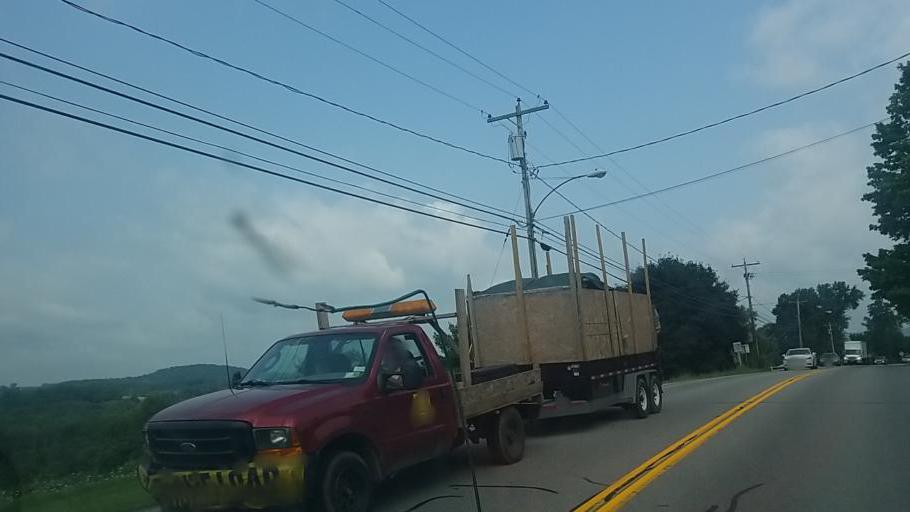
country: US
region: New York
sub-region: Montgomery County
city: Fort Plain
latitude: 42.9437
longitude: -74.6195
